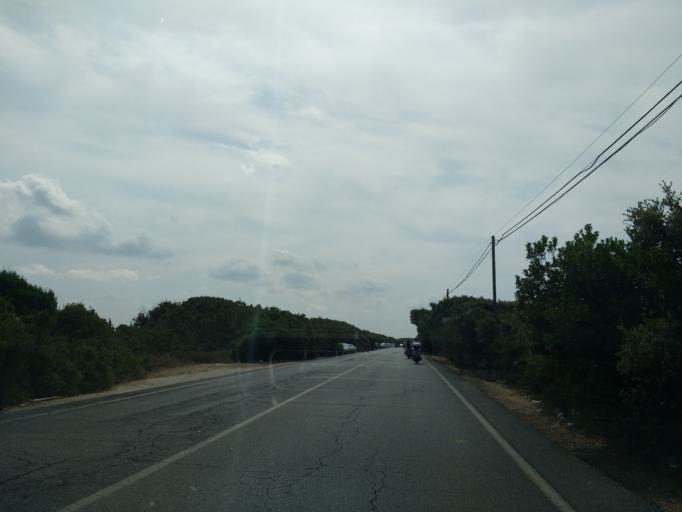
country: IT
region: Latium
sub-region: Citta metropolitana di Roma Capitale
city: Torvaianica
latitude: 41.6810
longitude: 12.3834
